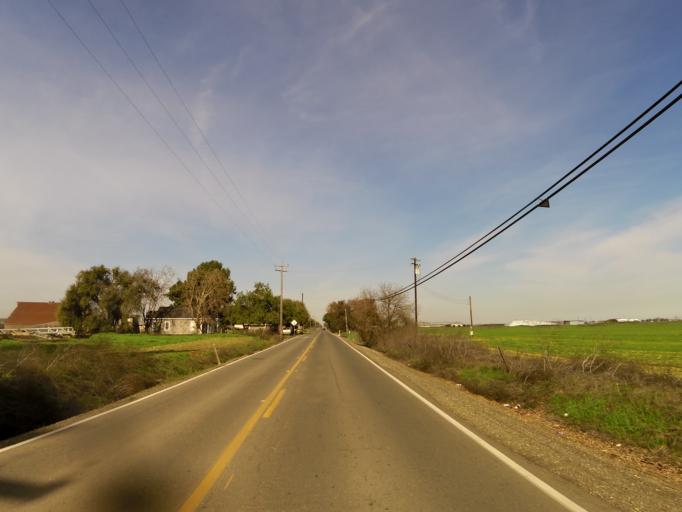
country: US
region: California
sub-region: San Joaquin County
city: Thornton
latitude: 38.3221
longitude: -121.4171
